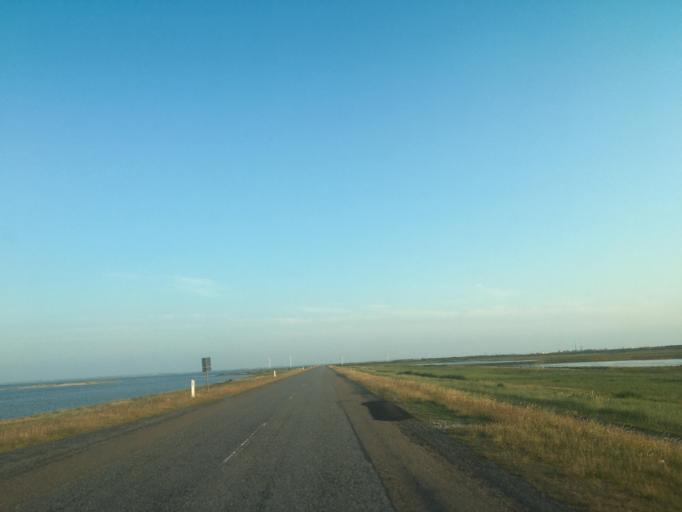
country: DK
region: Central Jutland
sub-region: Lemvig Kommune
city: Thyboron
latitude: 56.7316
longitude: 8.2498
